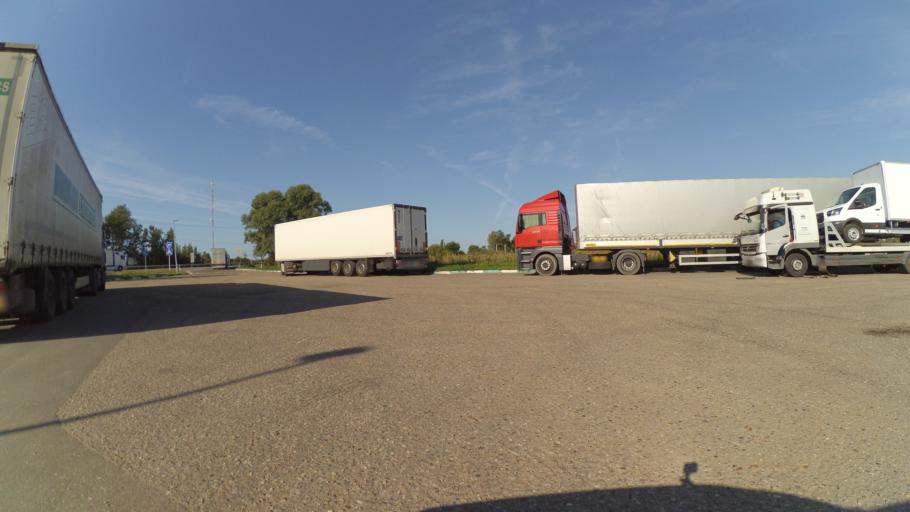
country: RU
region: Smolensk
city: Gagarin
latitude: 55.5013
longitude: 35.1780
